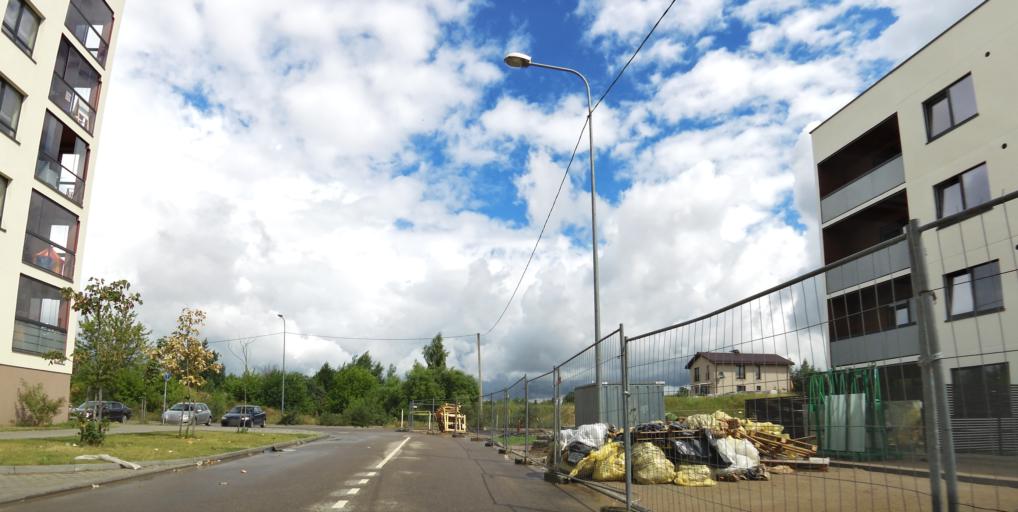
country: LT
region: Vilnius County
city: Pilaite
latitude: 54.7139
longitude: 25.1844
